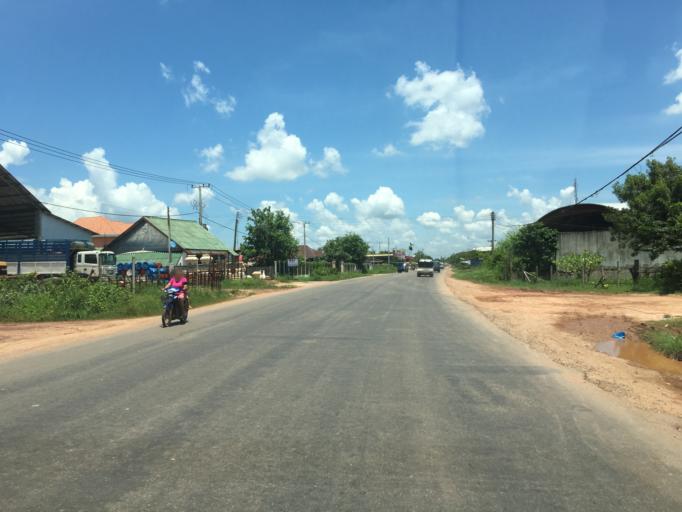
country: LA
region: Vientiane
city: Vientiane
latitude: 18.0964
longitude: 102.5099
